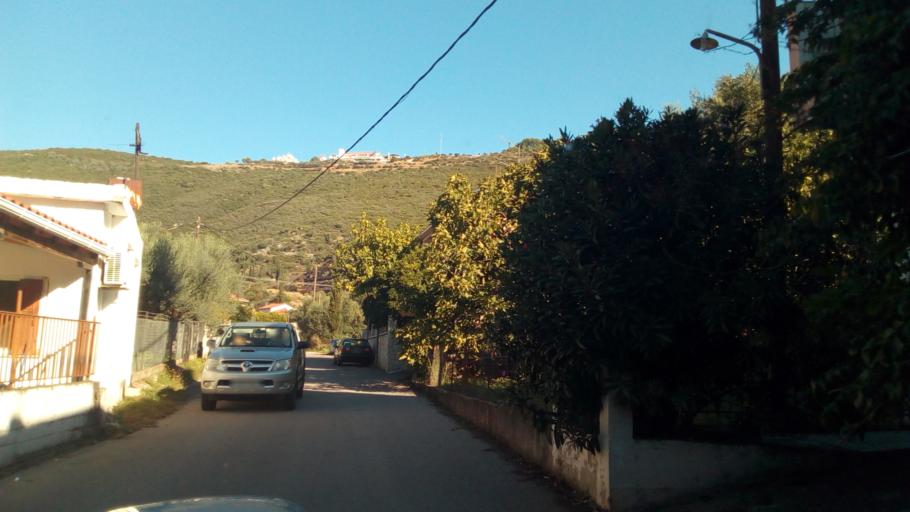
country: GR
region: West Greece
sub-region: Nomos Aitolias kai Akarnanias
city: Nafpaktos
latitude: 38.4077
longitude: 21.8546
